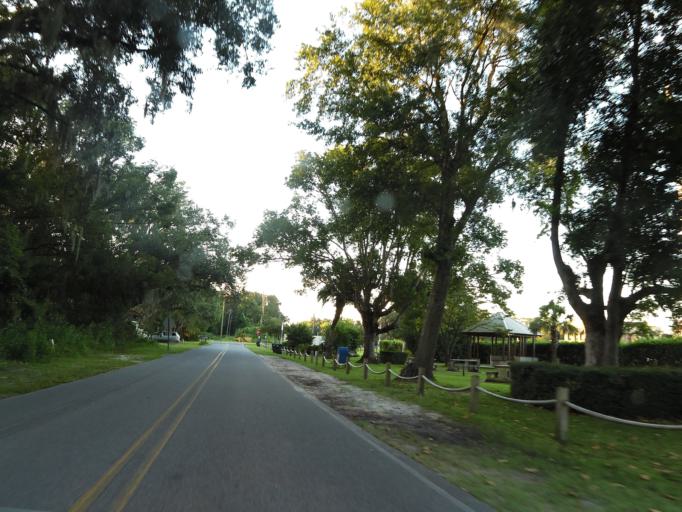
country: US
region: Georgia
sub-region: Camden County
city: Kingsland
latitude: 30.7987
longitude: -81.6915
